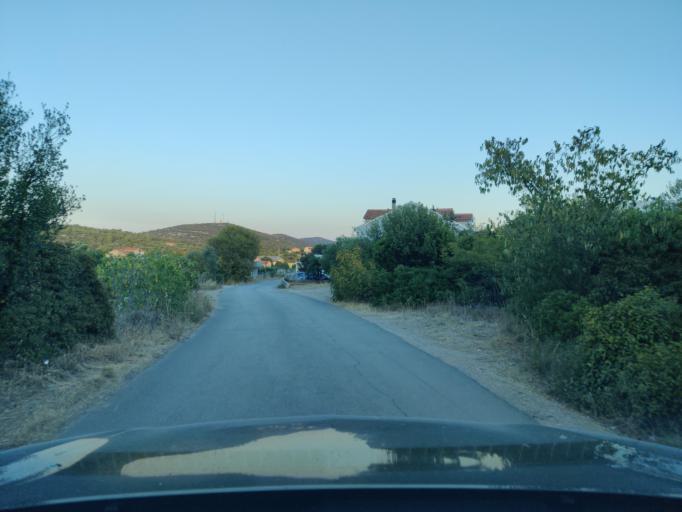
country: HR
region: Sibensko-Kniniska
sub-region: Grad Sibenik
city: Tisno
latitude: 43.8057
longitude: 15.6456
